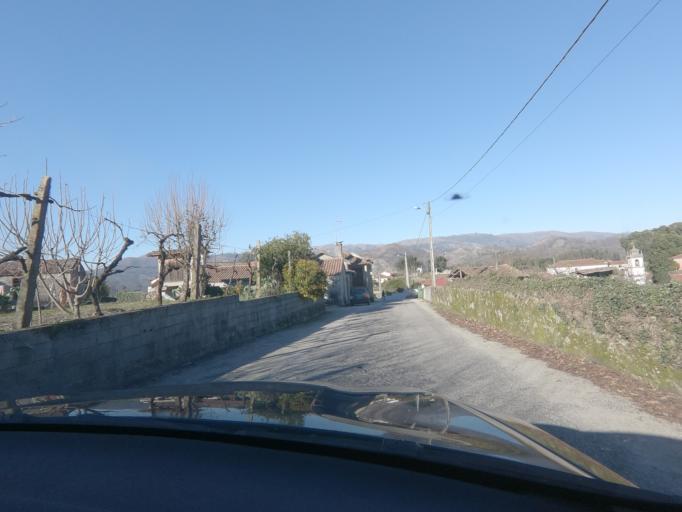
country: PT
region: Viseu
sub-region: Oliveira de Frades
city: Oliveira de Frades
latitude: 40.7323
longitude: -8.1573
